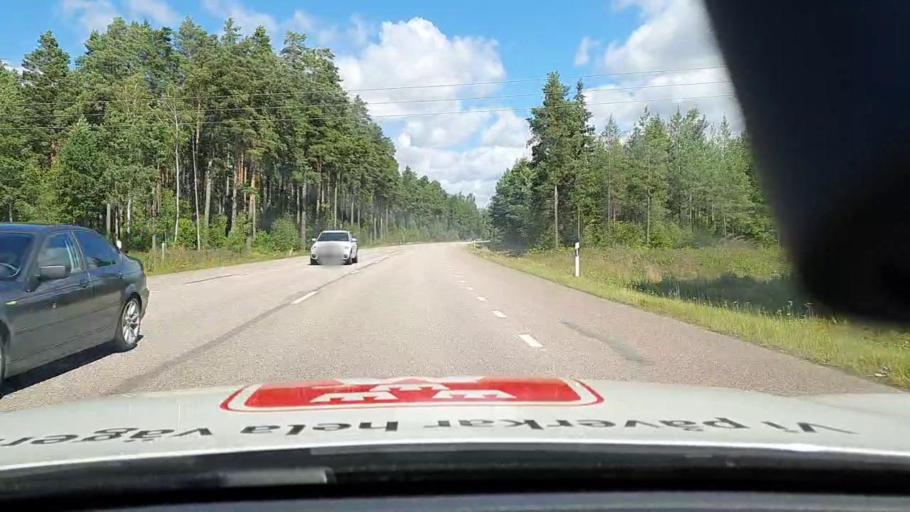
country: SE
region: Vaestra Goetaland
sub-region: Skovde Kommun
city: Stopen
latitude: 58.4308
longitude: 13.9163
